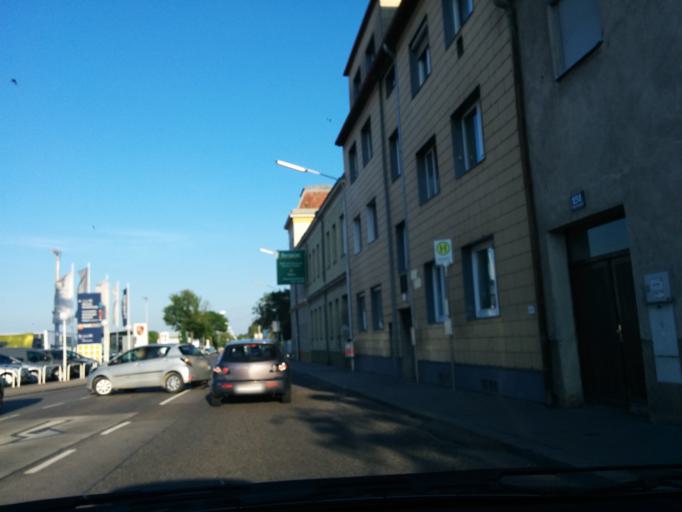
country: AT
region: Lower Austria
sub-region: Politischer Bezirk Modling
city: Brunn am Gebirge
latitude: 48.1294
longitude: 16.2983
